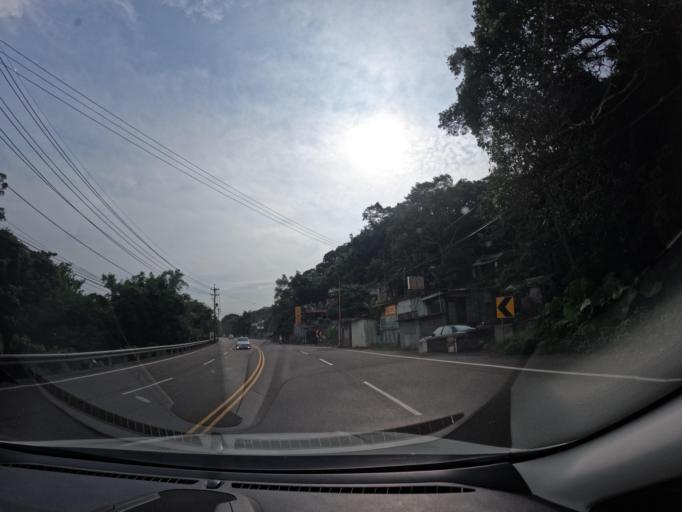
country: TW
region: Taiwan
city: Daxi
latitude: 24.8956
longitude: 121.3129
